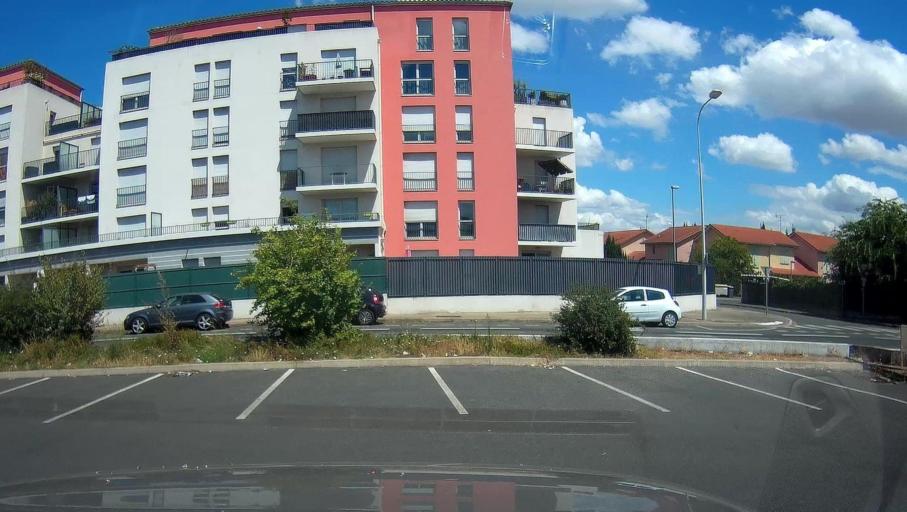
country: FR
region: Rhone-Alpes
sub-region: Departement du Rhone
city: Villefranche-sur-Saone
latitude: 45.9863
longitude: 4.7319
